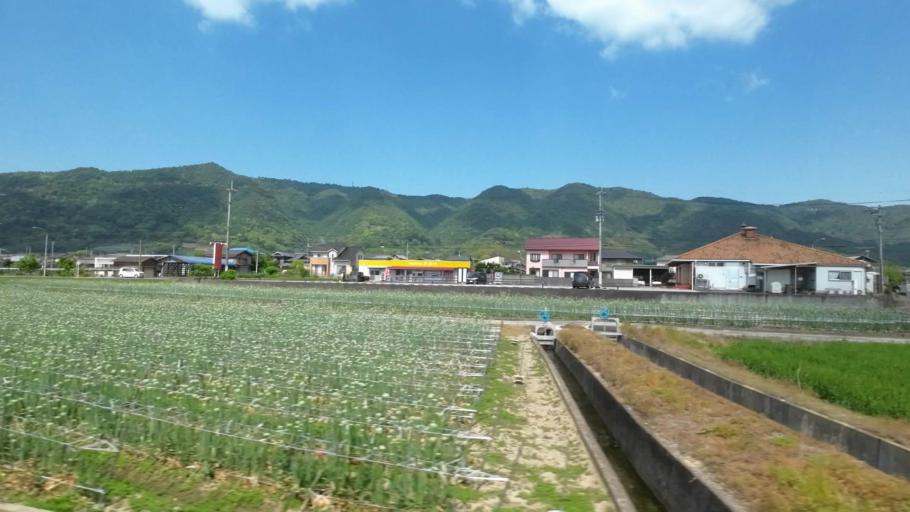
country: JP
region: Kagawa
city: Kan'onjicho
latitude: 34.1646
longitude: 133.6899
